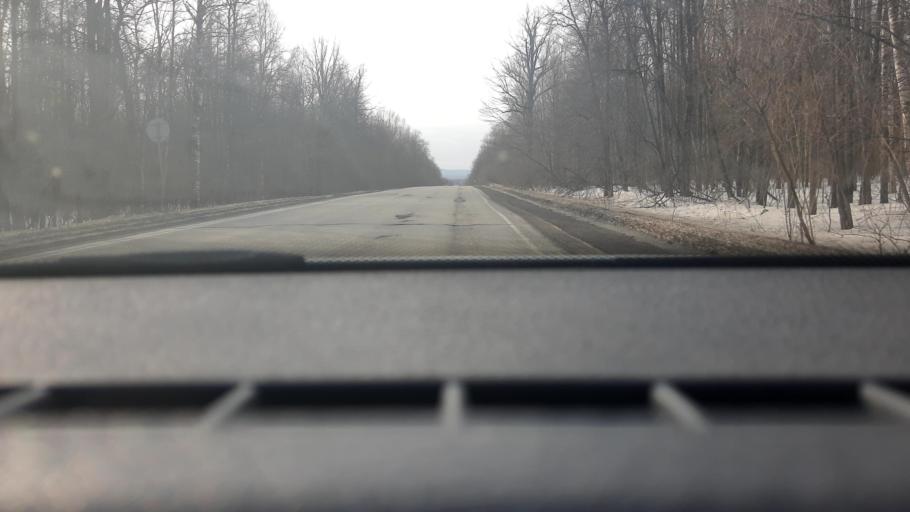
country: RU
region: Chelyabinsk
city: Asha
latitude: 54.9085
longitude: 57.2945
